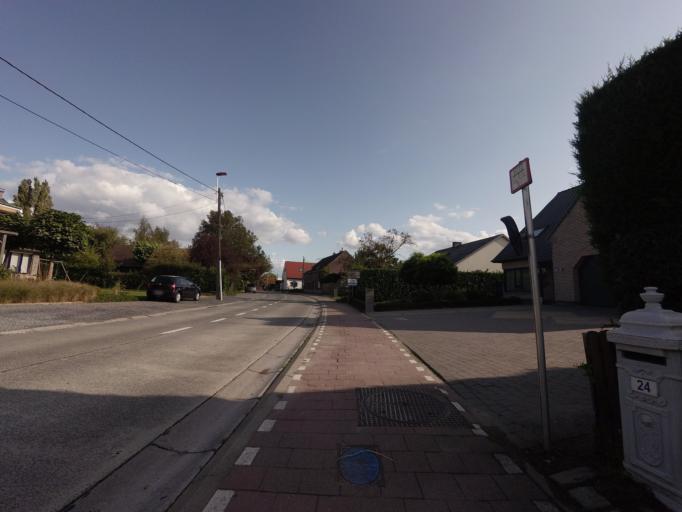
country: BE
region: Flanders
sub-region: Provincie Vlaams-Brabant
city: Londerzeel
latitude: 50.9797
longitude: 4.3303
